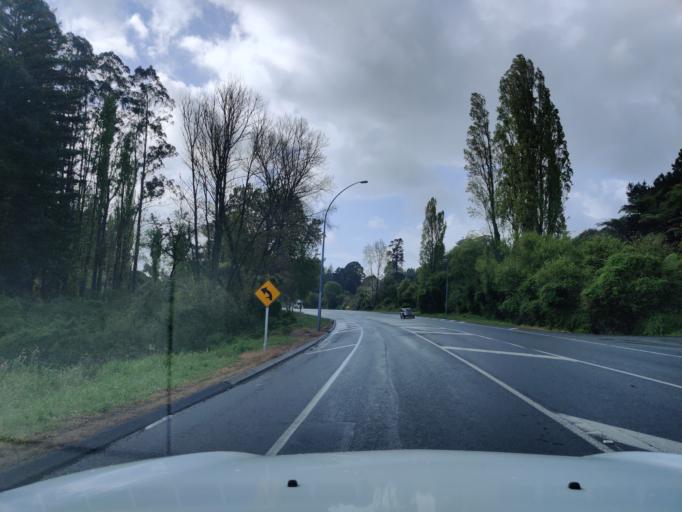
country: NZ
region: Waikato
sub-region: Hamilton City
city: Hamilton
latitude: -37.8088
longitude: 175.3346
